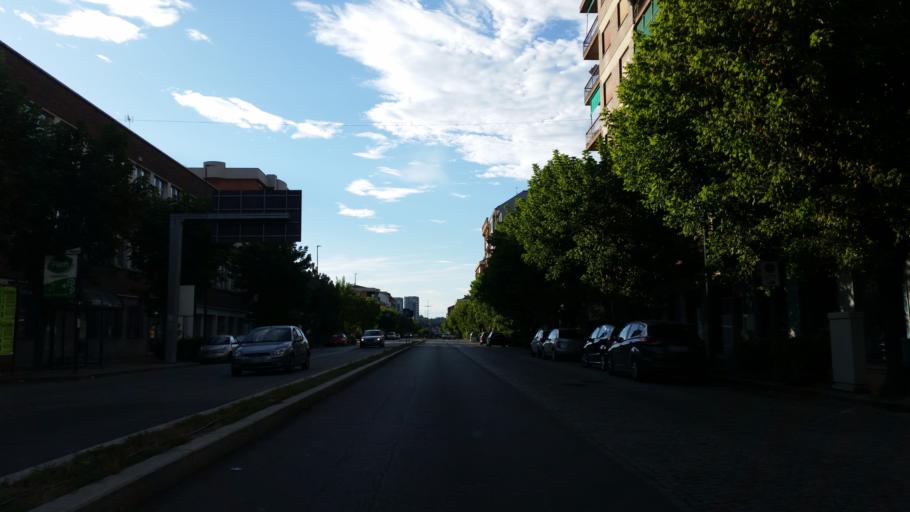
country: IT
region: Piedmont
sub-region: Provincia di Asti
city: Asti
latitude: 44.9008
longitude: 8.1931
